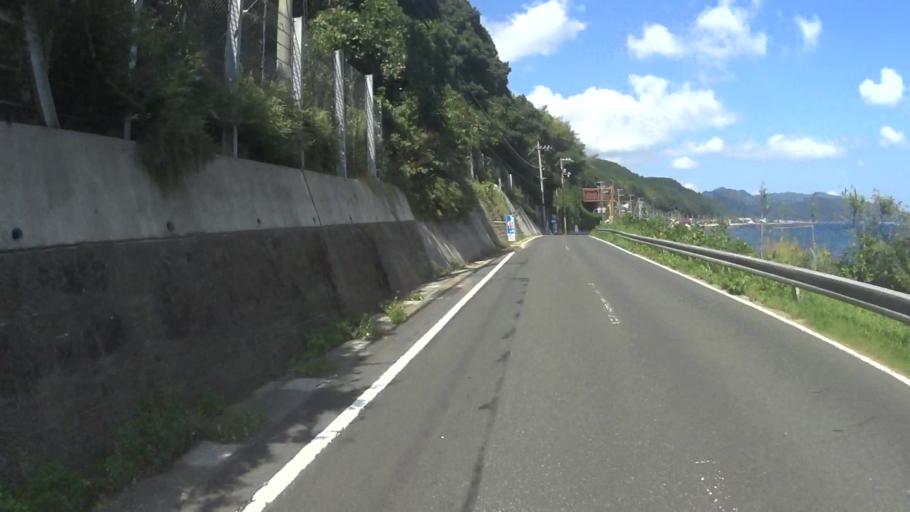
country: JP
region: Kyoto
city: Miyazu
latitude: 35.6448
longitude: 135.2506
